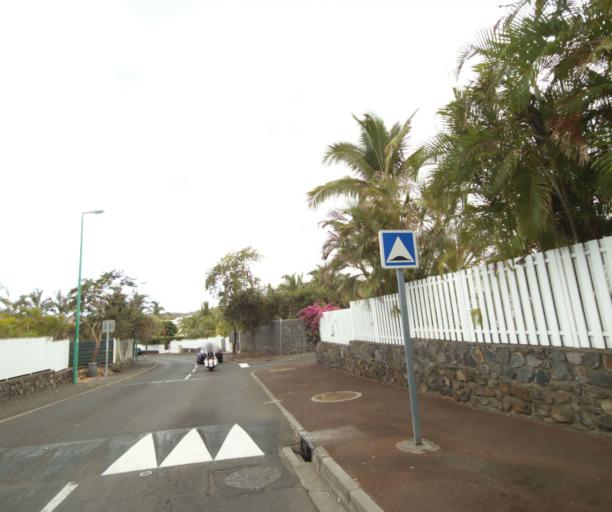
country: RE
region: Reunion
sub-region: Reunion
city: Saint-Paul
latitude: -21.0594
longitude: 55.2269
